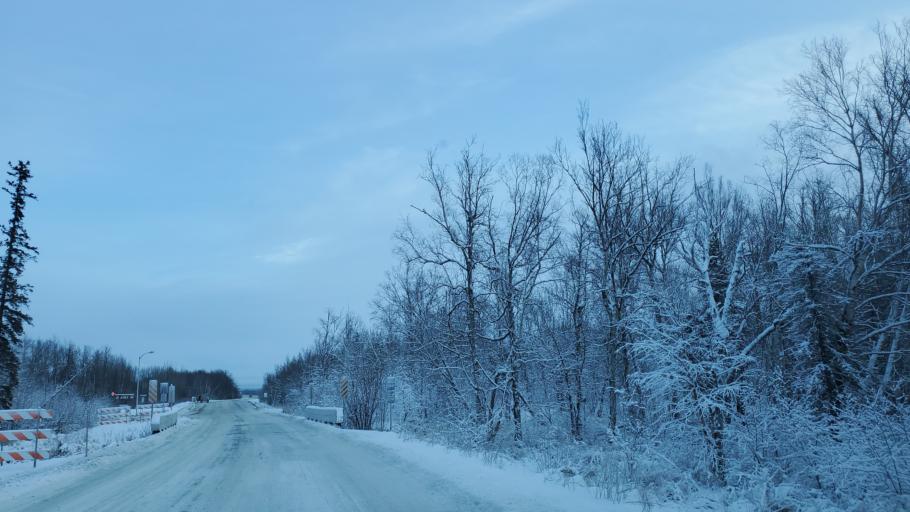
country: US
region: Alaska
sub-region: Matanuska-Susitna Borough
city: Lakes
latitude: 61.5507
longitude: -149.2948
